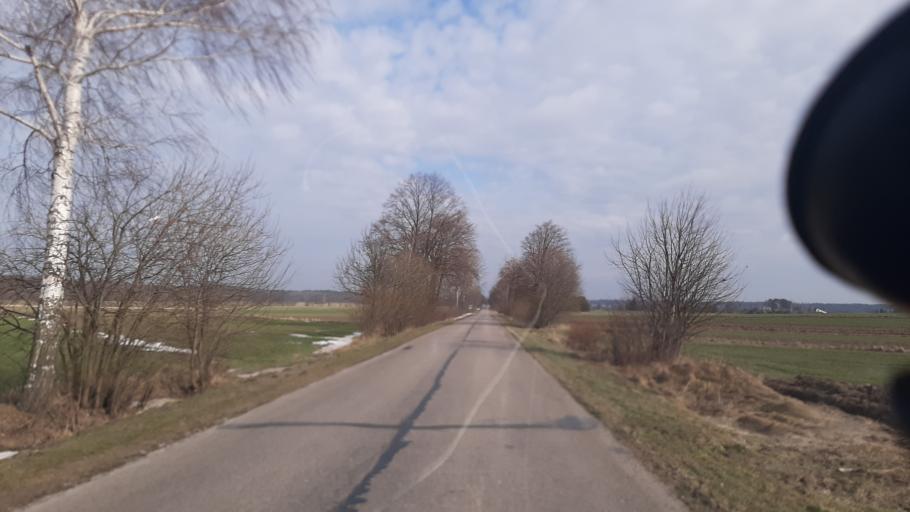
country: PL
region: Lublin Voivodeship
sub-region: Powiat lubartowski
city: Wola Sernicka
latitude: 51.4623
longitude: 22.7109
